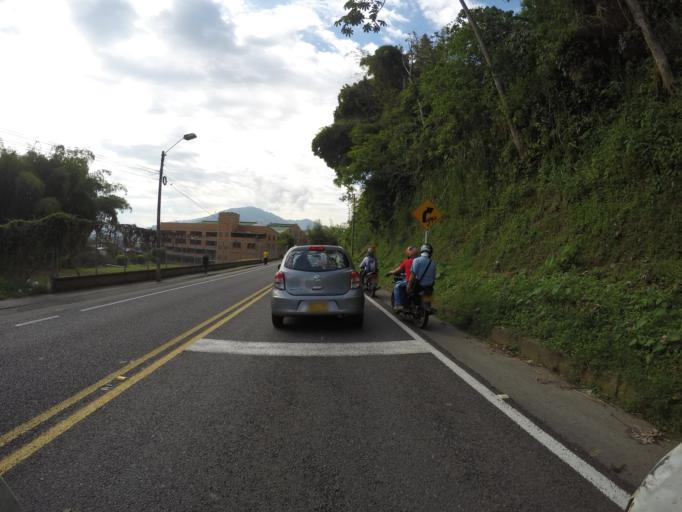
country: CO
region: Risaralda
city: Pereira
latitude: 4.7970
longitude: -75.6947
